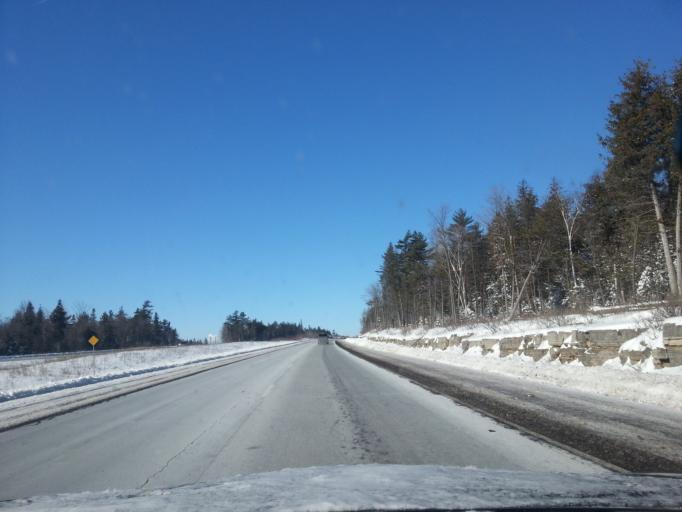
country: CA
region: Ontario
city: Arnprior
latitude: 45.3363
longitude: -76.1787
